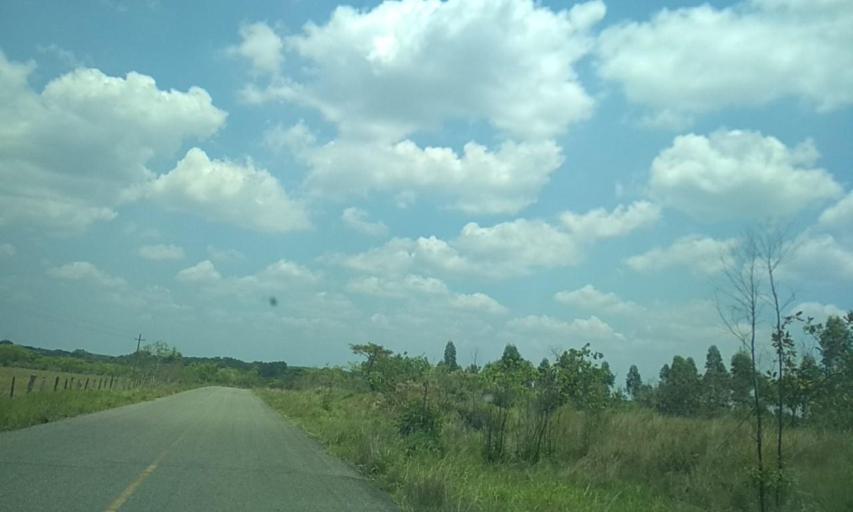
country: MX
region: Tabasco
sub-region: Huimanguillo
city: Francisco Rueda
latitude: 17.7917
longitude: -93.8422
